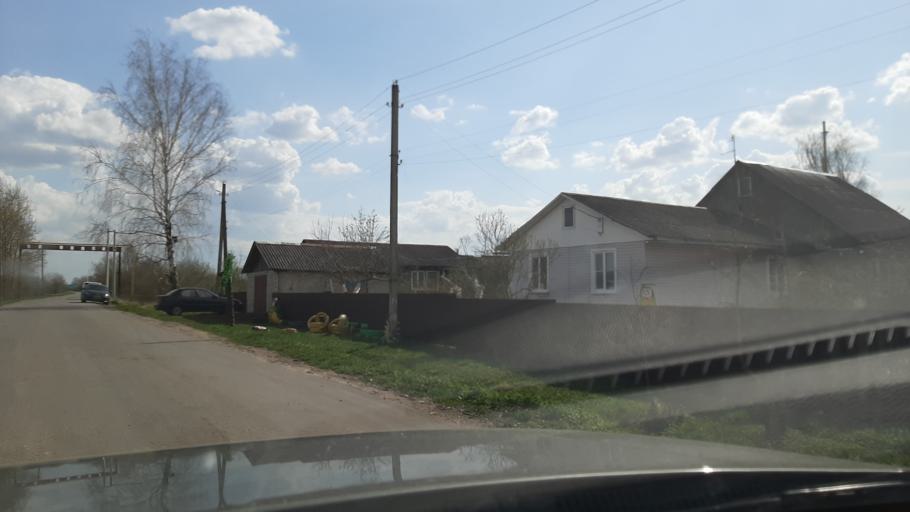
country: RU
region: Ivanovo
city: Privolzhsk
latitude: 57.3300
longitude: 41.2345
